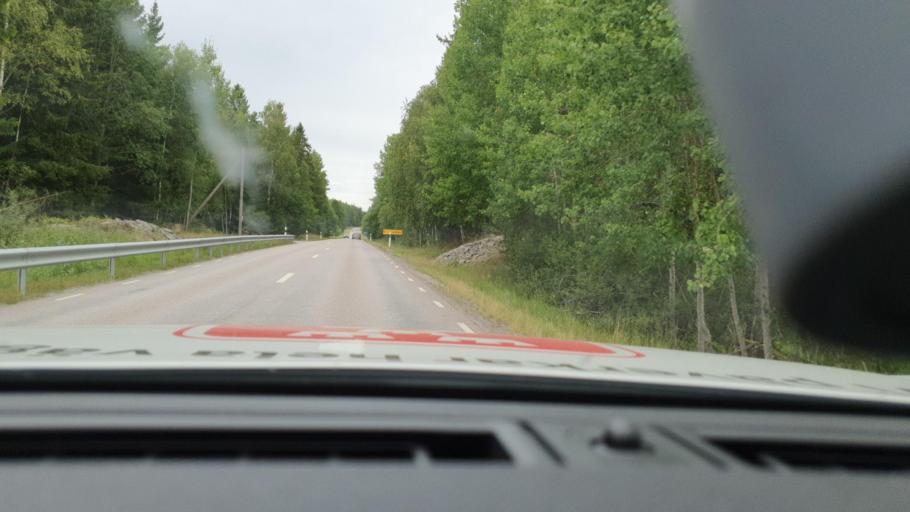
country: SE
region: Uppsala
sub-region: Heby Kommun
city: OEstervala
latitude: 59.9961
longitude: 17.3135
